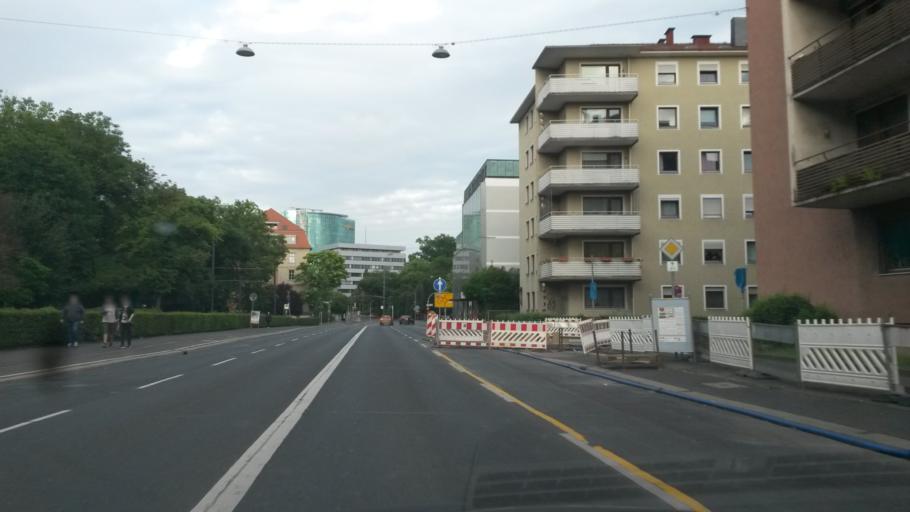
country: DE
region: Bavaria
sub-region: Regierungsbezirk Unterfranken
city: Wuerzburg
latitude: 49.7997
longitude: 9.9395
